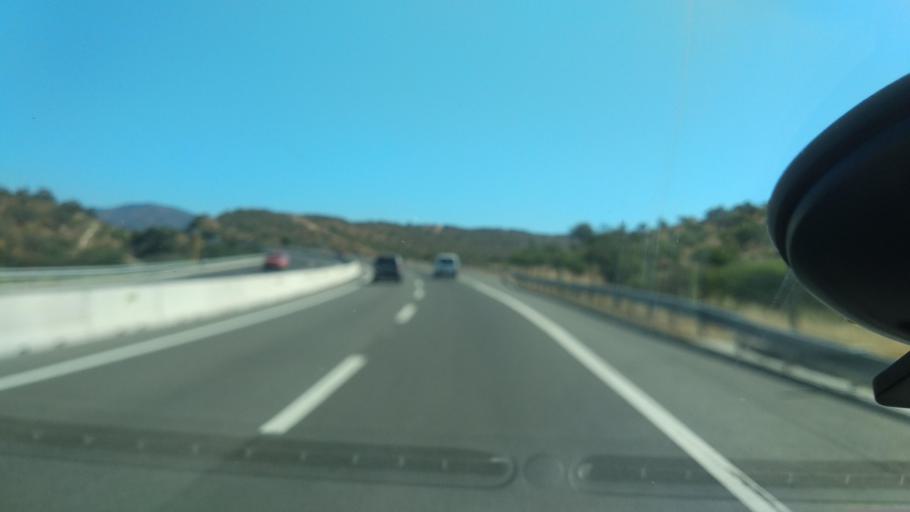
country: CL
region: Valparaiso
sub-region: Provincia de Marga Marga
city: Limache
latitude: -33.0298
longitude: -71.3197
